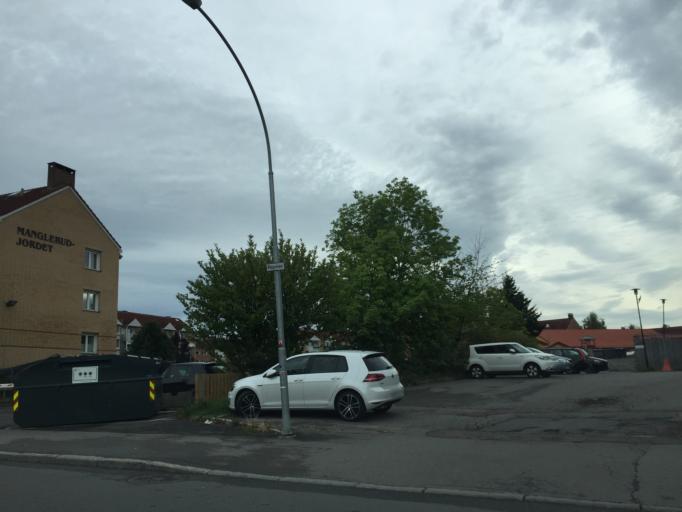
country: NO
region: Oslo
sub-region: Oslo
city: Oslo
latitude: 59.8967
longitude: 10.8140
